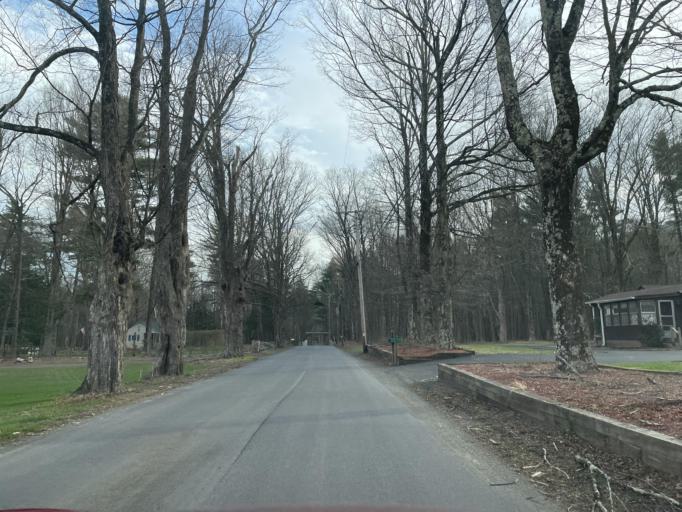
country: US
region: New York
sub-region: Greene County
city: Palenville
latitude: 42.1691
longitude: -74.0215
